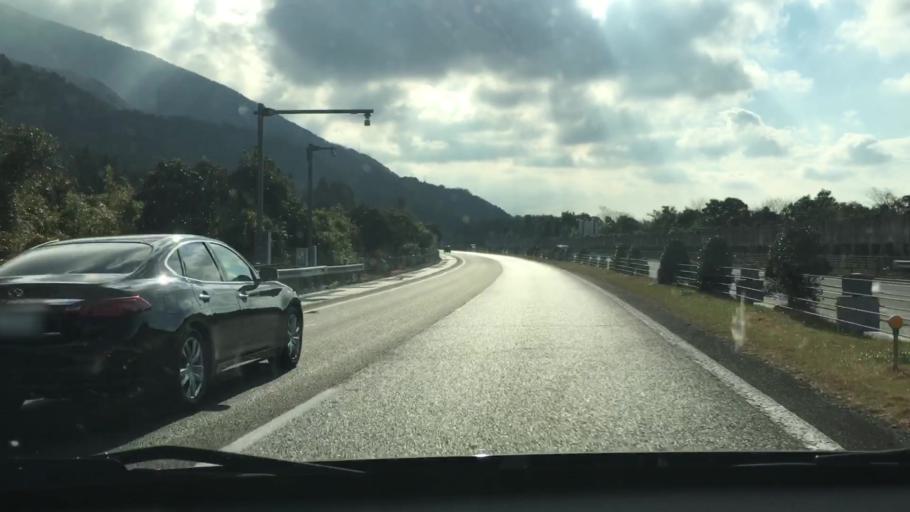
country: JP
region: Kumamoto
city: Yatsushiro
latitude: 32.5375
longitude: 130.6735
